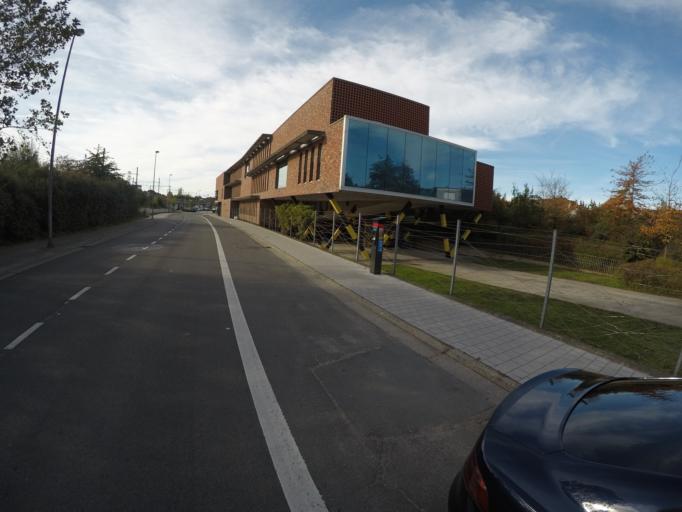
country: BE
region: Flanders
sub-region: Provincie Oost-Vlaanderen
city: Sint-Niklaas
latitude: 51.1714
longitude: 4.1416
